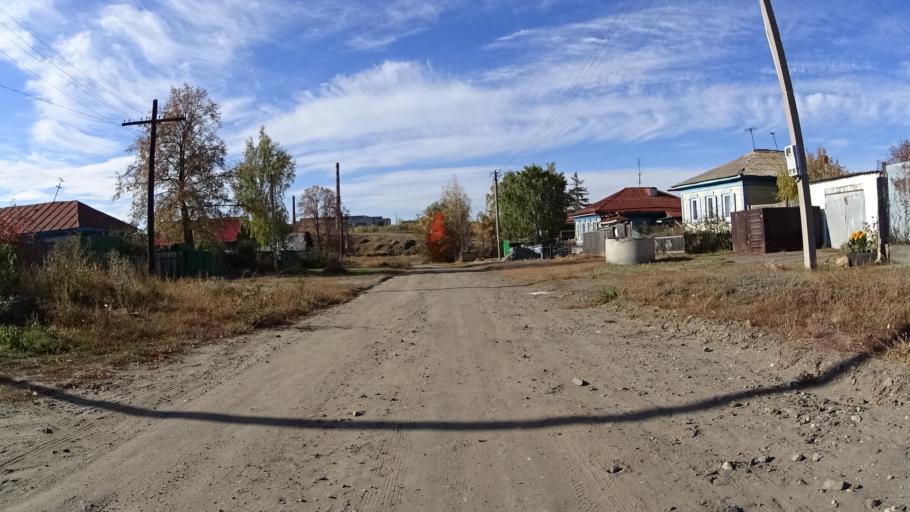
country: RU
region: Chelyabinsk
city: Troitsk
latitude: 54.0742
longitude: 61.5821
